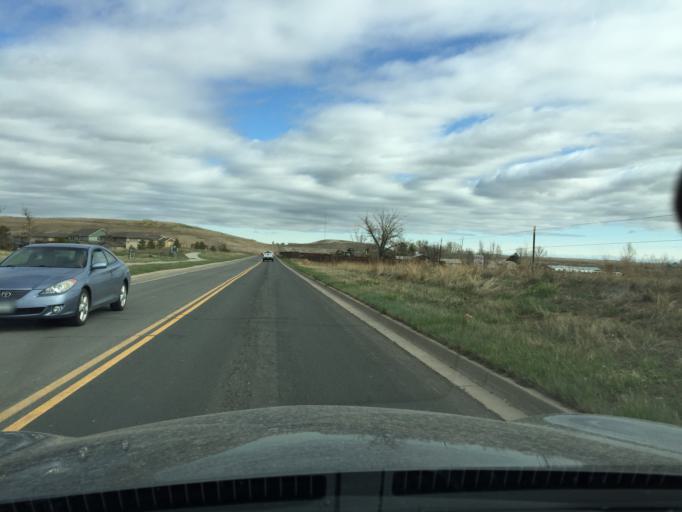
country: US
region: Colorado
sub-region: Boulder County
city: Erie
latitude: 40.0081
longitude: -105.0086
